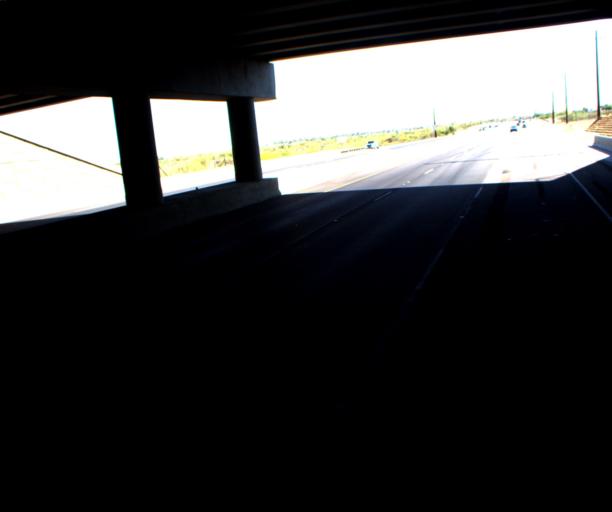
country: US
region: Arizona
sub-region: Pima County
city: Catalina
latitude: 32.4681
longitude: -110.9251
